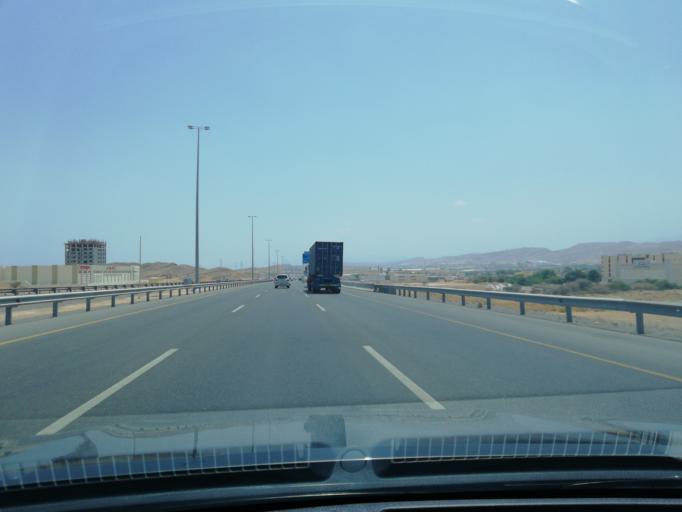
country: OM
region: Muhafazat Masqat
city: As Sib al Jadidah
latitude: 23.5691
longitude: 58.1728
